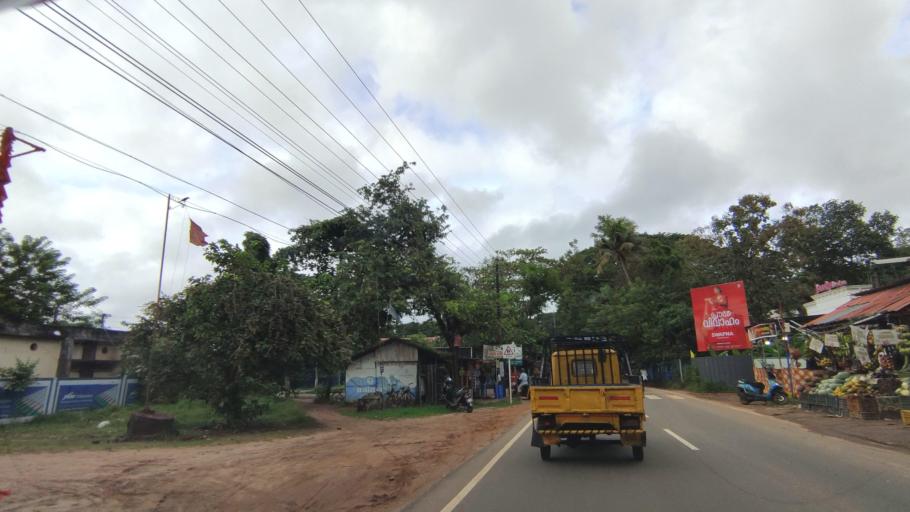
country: IN
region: Kerala
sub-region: Alappuzha
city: Shertallai
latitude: 9.6144
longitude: 76.3631
